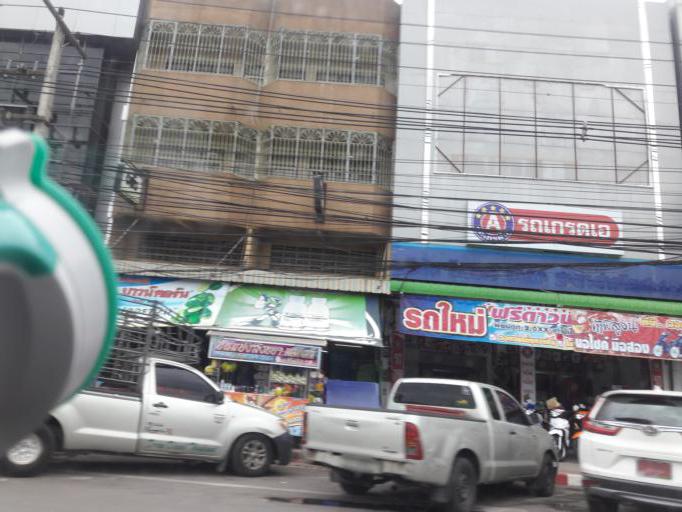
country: TH
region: Ratchaburi
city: Damnoen Saduak
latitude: 13.5300
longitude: 99.9678
